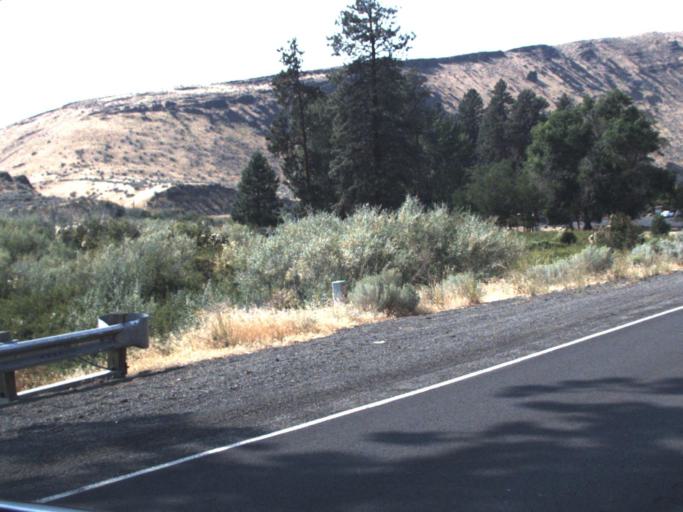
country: US
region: Washington
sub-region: Yakima County
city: Selah
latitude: 46.7922
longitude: -120.4538
